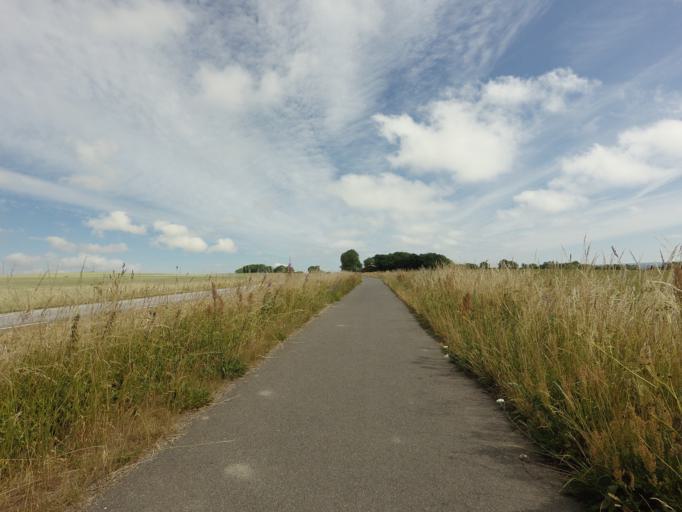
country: SE
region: Skane
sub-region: Simrishamns Kommun
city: Simrishamn
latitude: 55.5058
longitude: 14.3322
